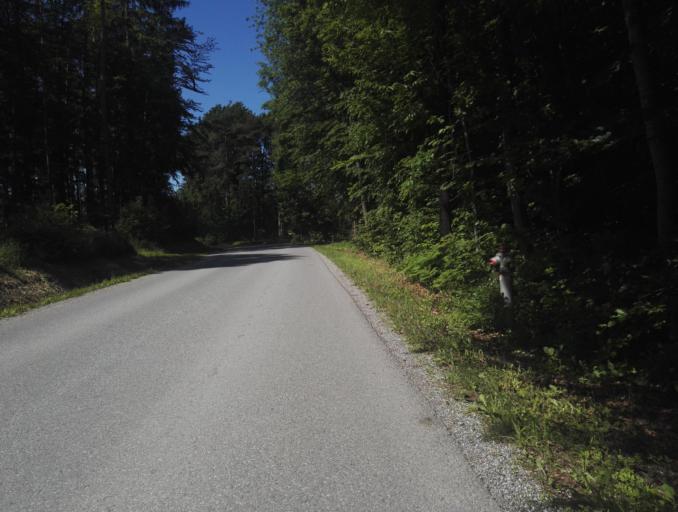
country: AT
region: Styria
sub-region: Politischer Bezirk Graz-Umgebung
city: Edelsgrub
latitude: 47.0516
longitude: 15.5737
